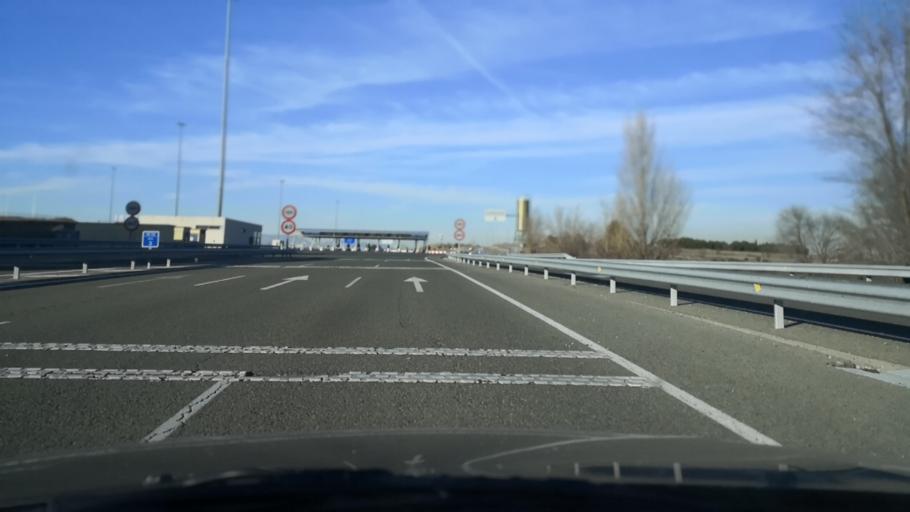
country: ES
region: Madrid
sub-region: Provincia de Madrid
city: Barajas de Madrid
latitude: 40.4740
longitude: -3.6012
